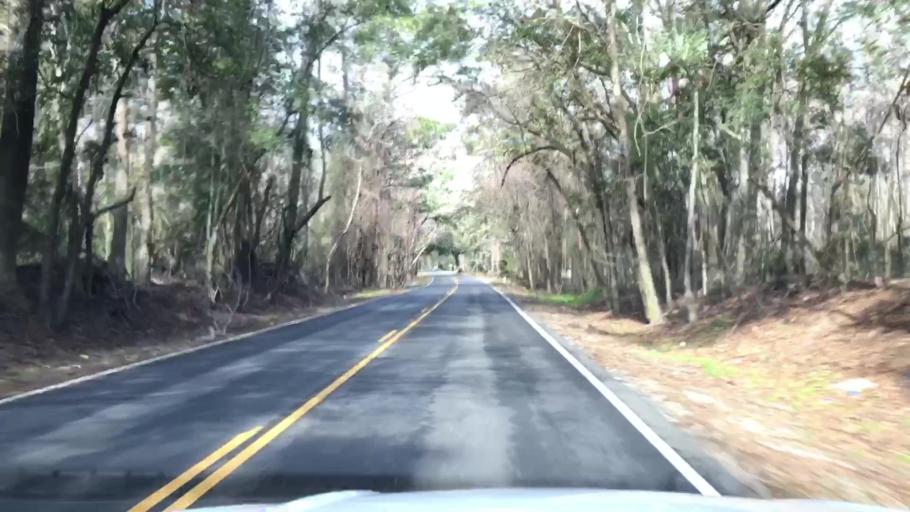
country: US
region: South Carolina
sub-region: Charleston County
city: Folly Beach
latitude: 32.7125
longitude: -80.0185
